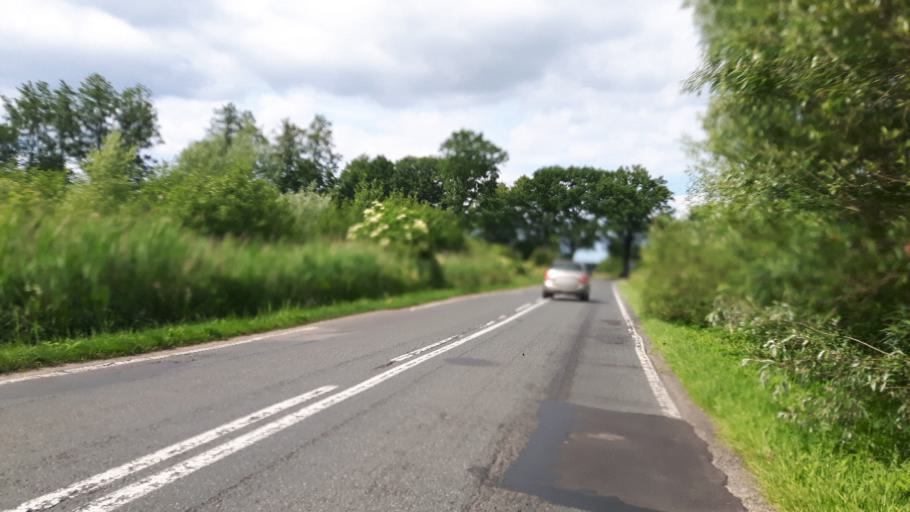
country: PL
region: West Pomeranian Voivodeship
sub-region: Szczecin
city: Szczecin
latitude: 53.4149
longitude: 14.7026
